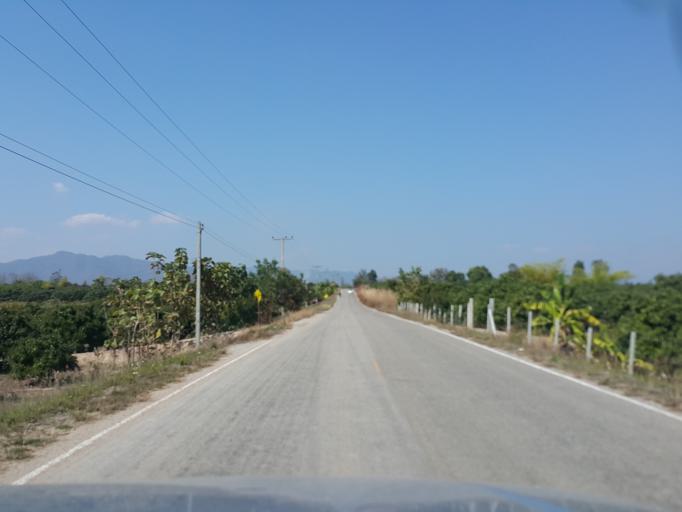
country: TH
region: Chiang Mai
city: Mae Wang
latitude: 18.5607
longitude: 98.7936
